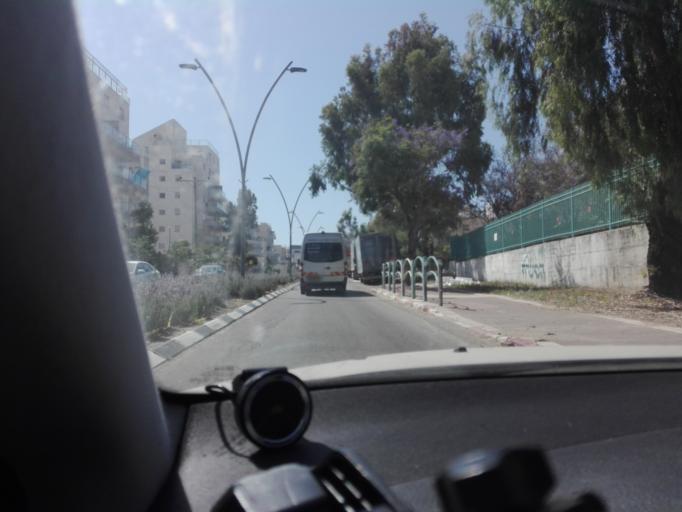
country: IL
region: Central District
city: Bene 'Ayish
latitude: 31.7237
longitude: 34.7452
